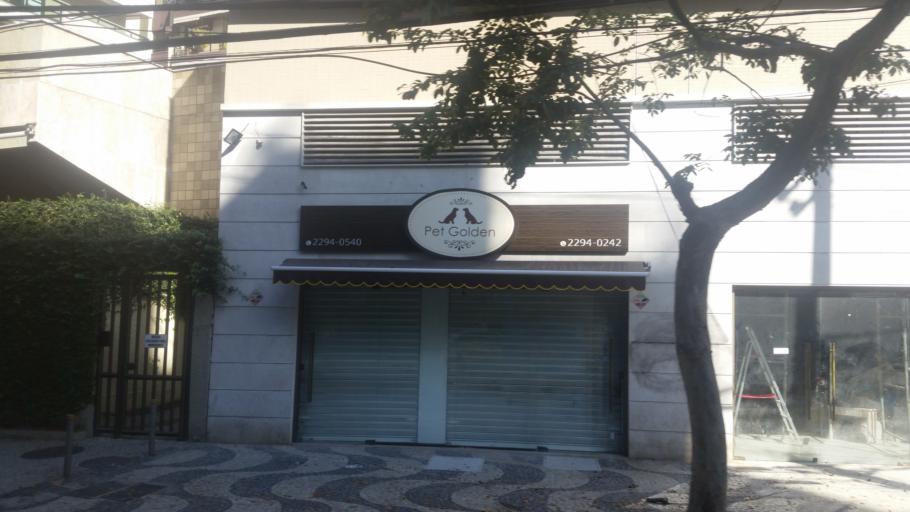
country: BR
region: Rio de Janeiro
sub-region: Rio De Janeiro
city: Rio de Janeiro
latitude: -22.9770
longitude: -43.2302
